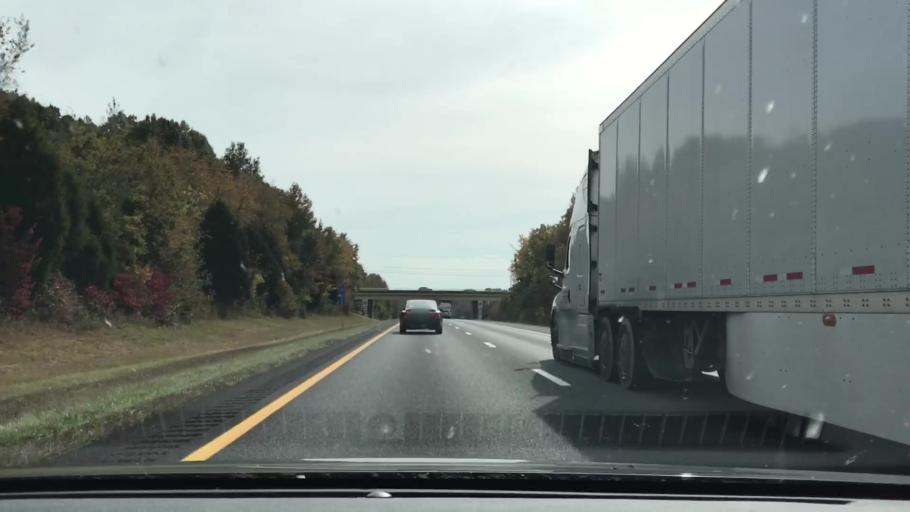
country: US
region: Tennessee
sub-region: Montgomery County
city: Clarksville
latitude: 36.5579
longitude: -87.2511
